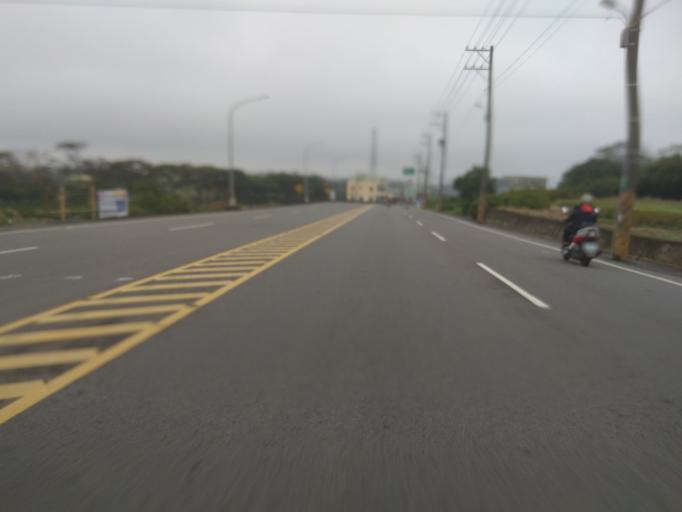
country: TW
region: Taiwan
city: Taoyuan City
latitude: 25.0176
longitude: 121.1258
